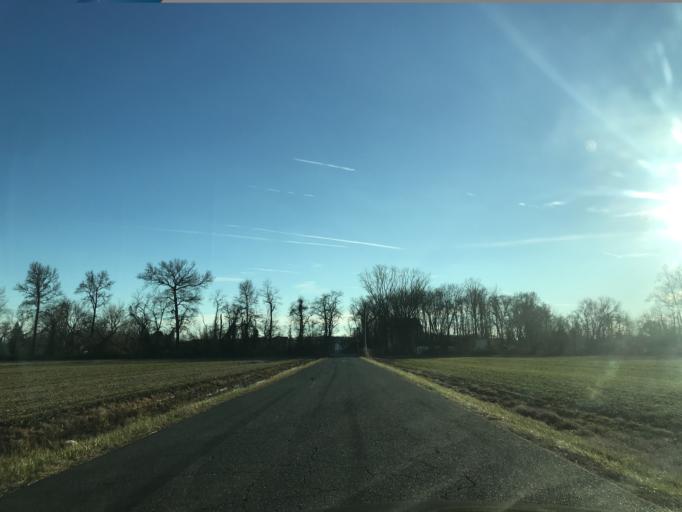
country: US
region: Maryland
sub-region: Baltimore County
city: Bowleys Quarters
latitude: 39.3274
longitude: -76.3781
